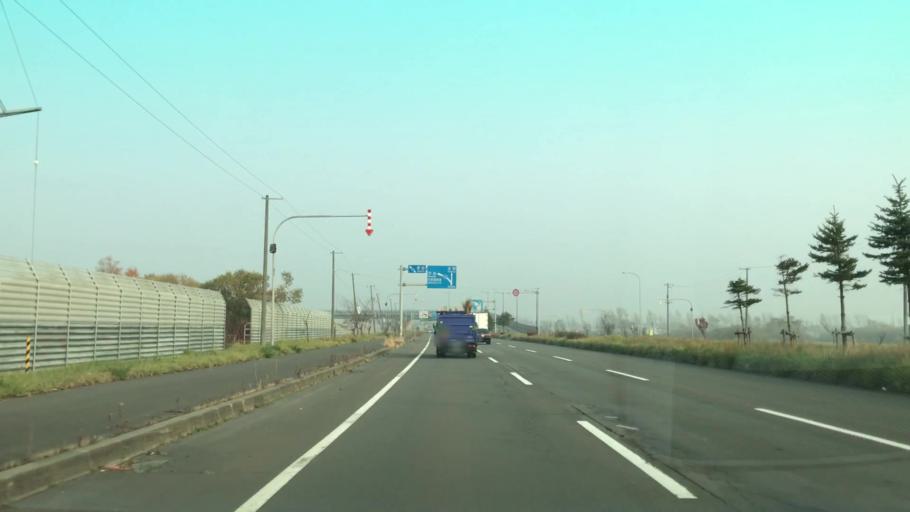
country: JP
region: Hokkaido
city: Ishikari
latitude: 43.1756
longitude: 141.3482
